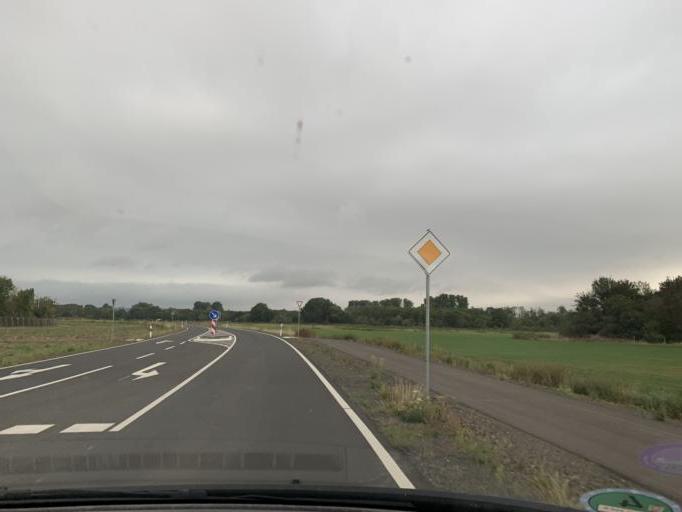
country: DE
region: North Rhine-Westphalia
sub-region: Regierungsbezirk Koln
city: Niederzier
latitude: 50.8434
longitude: 6.4356
